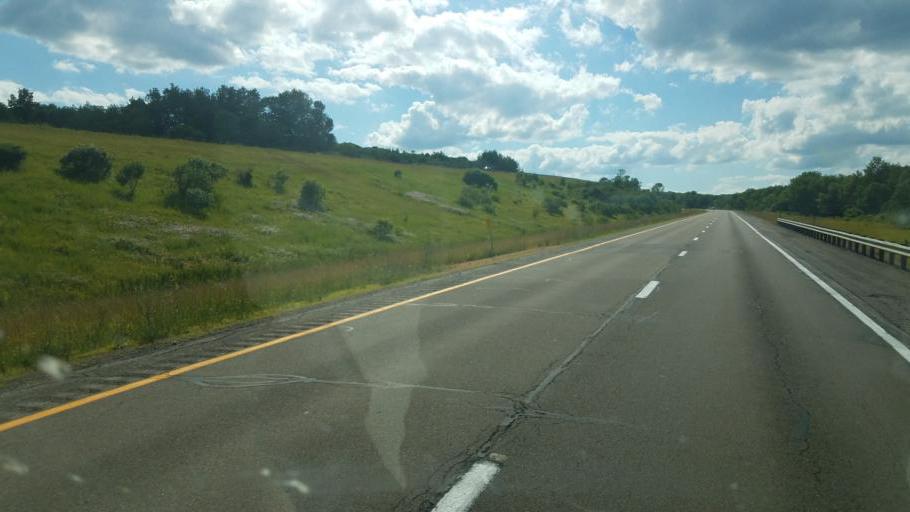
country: US
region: New York
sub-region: Allegany County
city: Alfred
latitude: 42.3188
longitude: -77.8238
